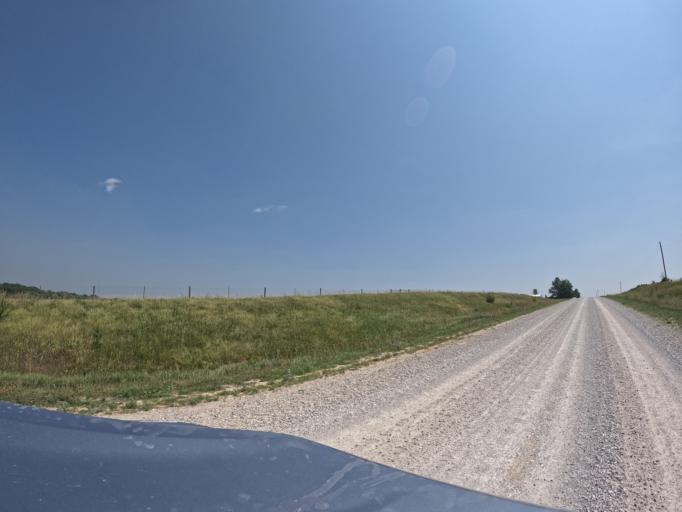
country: US
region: Iowa
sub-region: Keokuk County
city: Sigourney
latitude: 41.3467
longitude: -92.2388
